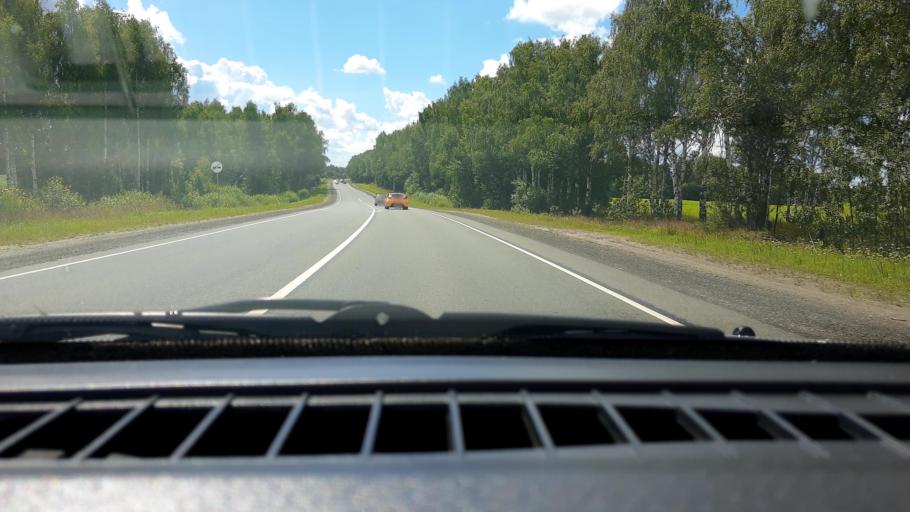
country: RU
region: Nizjnij Novgorod
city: Linda
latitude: 56.5965
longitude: 44.0389
